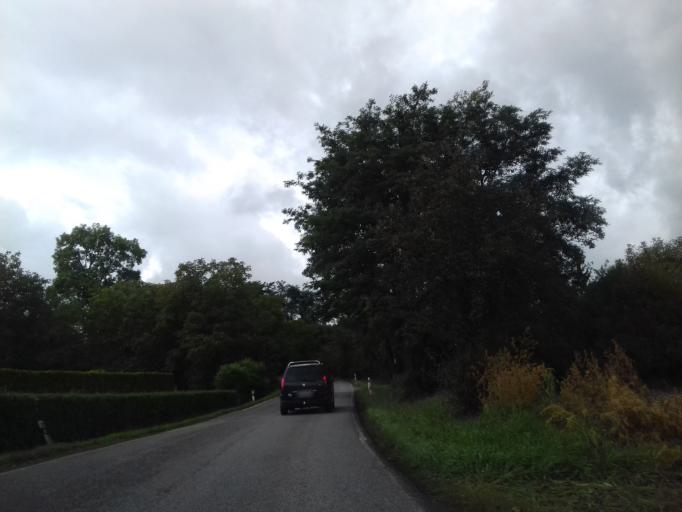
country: CZ
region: Central Bohemia
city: Revnice
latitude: 49.9241
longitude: 14.2469
